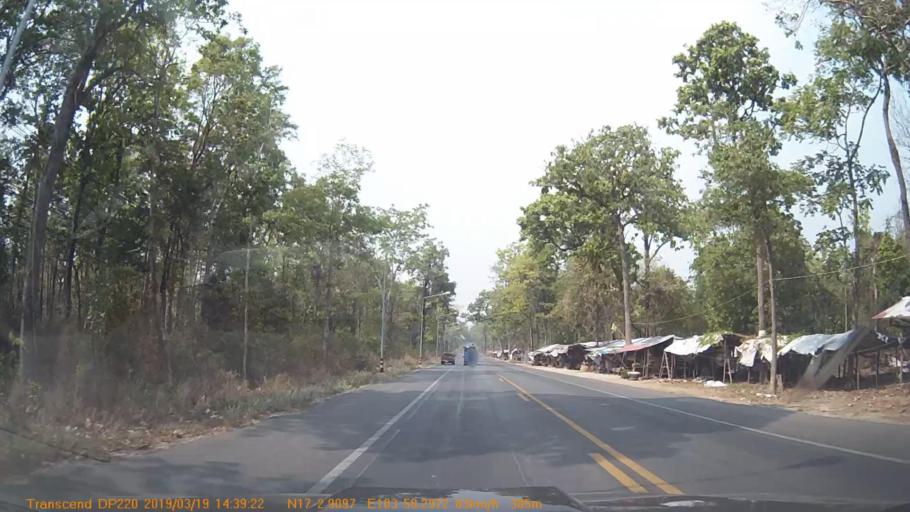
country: TH
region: Sakon Nakhon
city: Phu Phan
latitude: 17.0488
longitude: 103.9716
